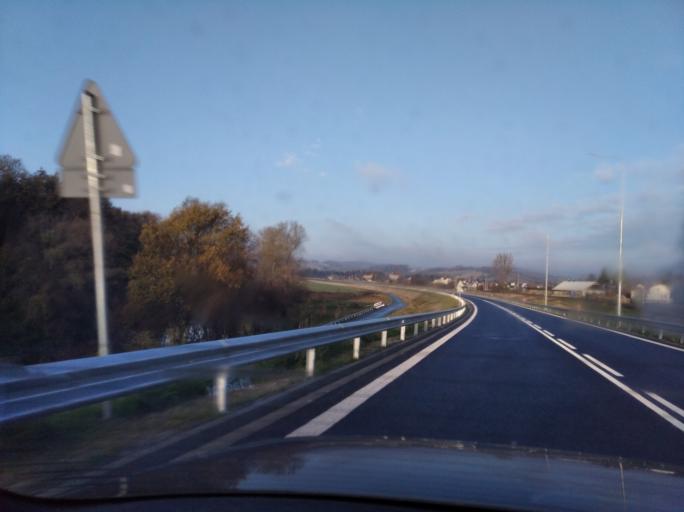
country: PL
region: Subcarpathian Voivodeship
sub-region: Powiat strzyzowski
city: Czudec
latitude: 49.9386
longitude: 21.8413
